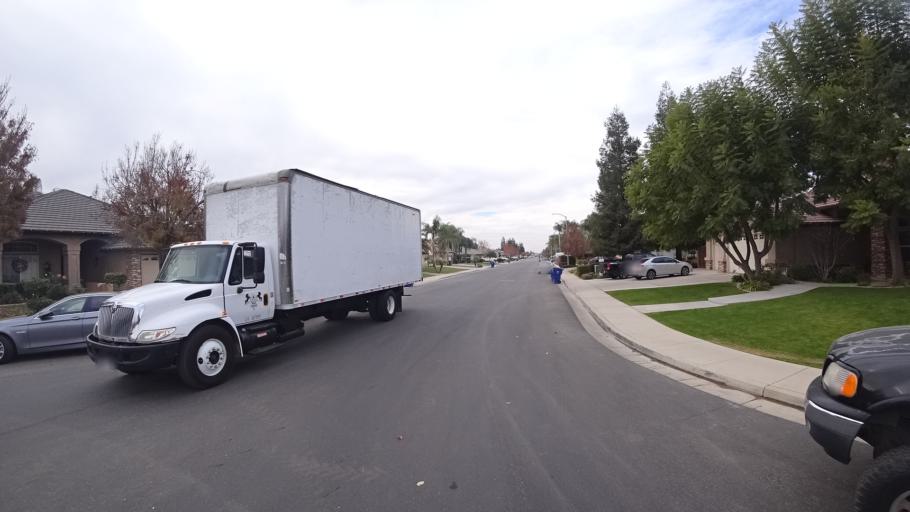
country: US
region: California
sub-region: Kern County
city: Rosedale
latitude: 35.4148
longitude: -119.1286
